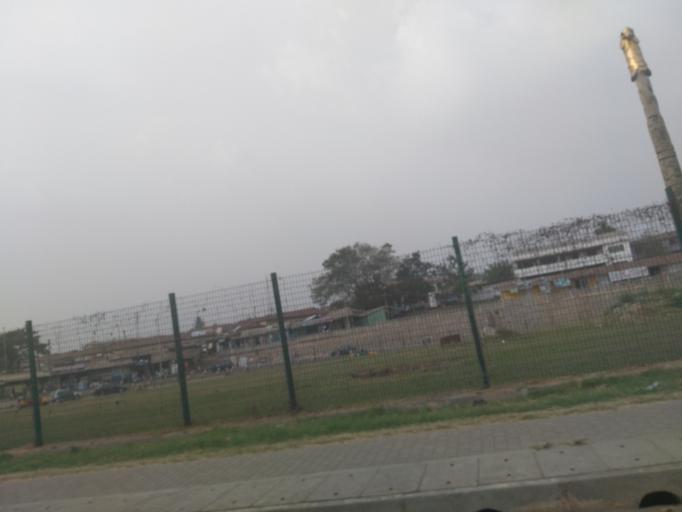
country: GH
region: Ashanti
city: Mamponteng
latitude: 6.6868
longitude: -1.5721
